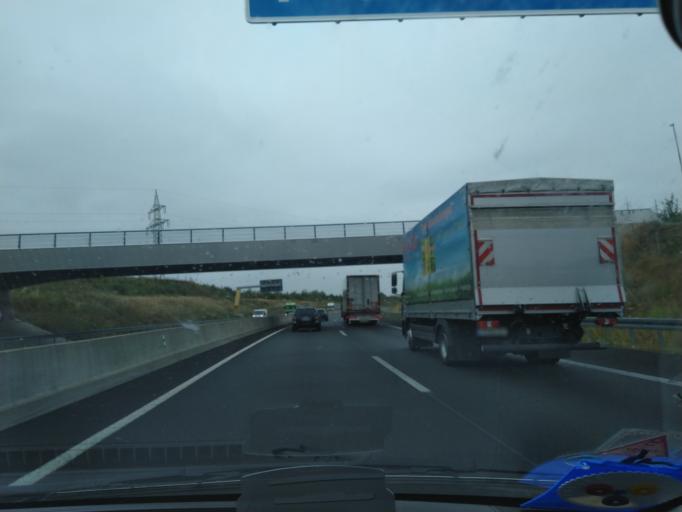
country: DE
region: North Rhine-Westphalia
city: Bad Oeynhausen
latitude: 52.2346
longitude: 8.8071
